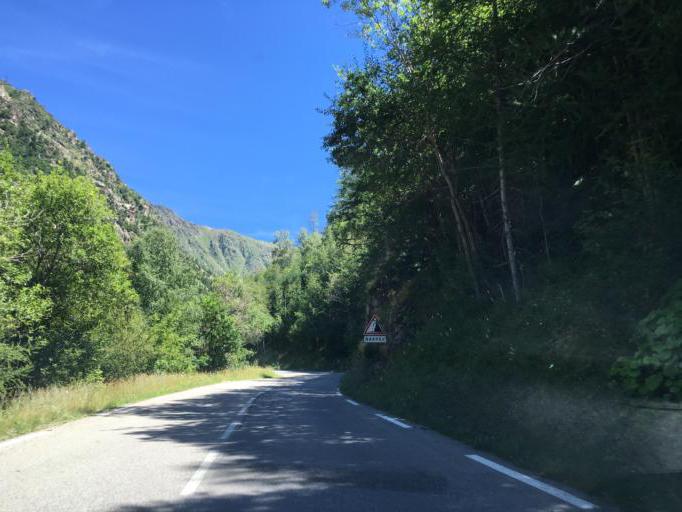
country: IT
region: Piedmont
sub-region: Provincia di Cuneo
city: Sambuco
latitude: 44.1999
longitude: 7.0789
